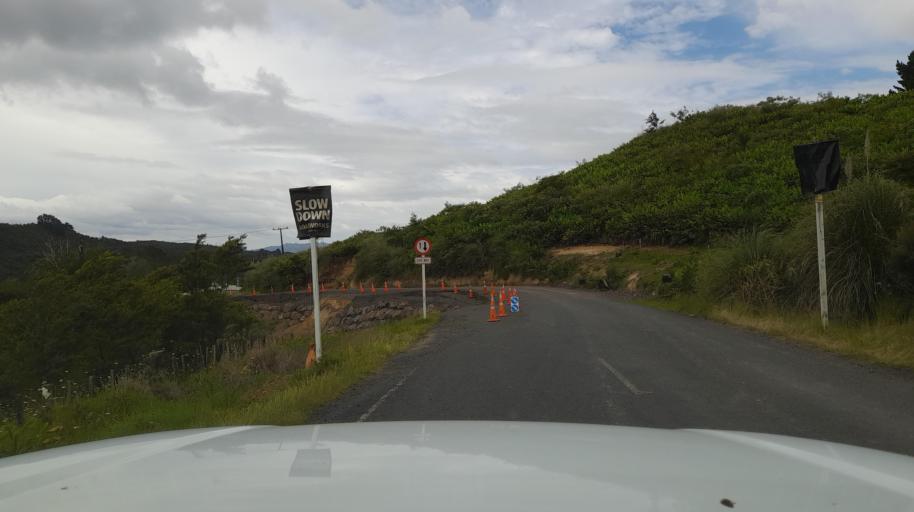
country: NZ
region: Northland
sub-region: Far North District
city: Kaitaia
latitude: -35.3743
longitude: 173.3801
